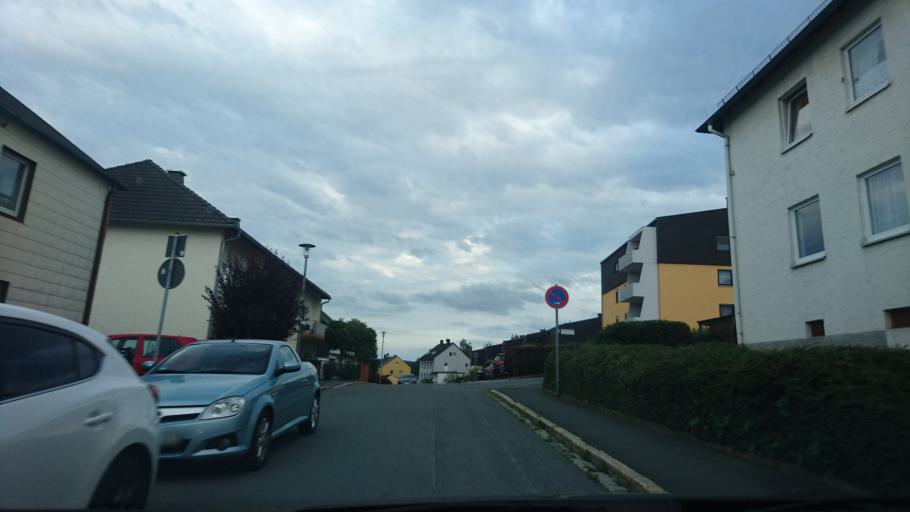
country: DE
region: Bavaria
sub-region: Upper Franconia
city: Naila
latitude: 50.3374
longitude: 11.7030
